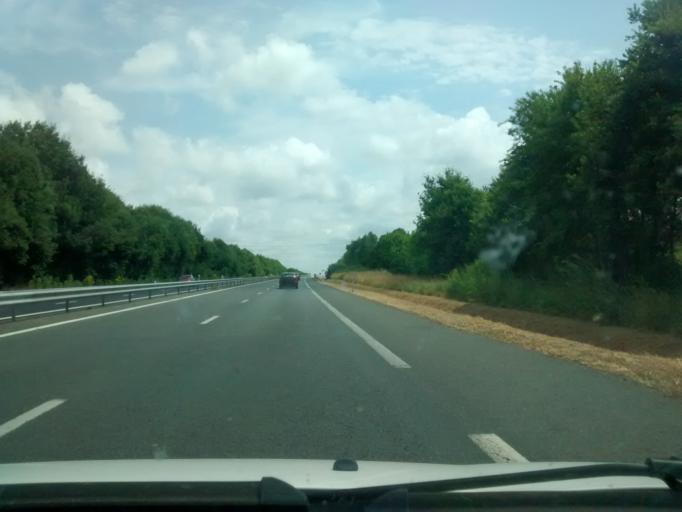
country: FR
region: Brittany
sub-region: Departement d'Ille-et-Vilaine
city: Roz-Landrieux
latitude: 48.5468
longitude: -1.8357
